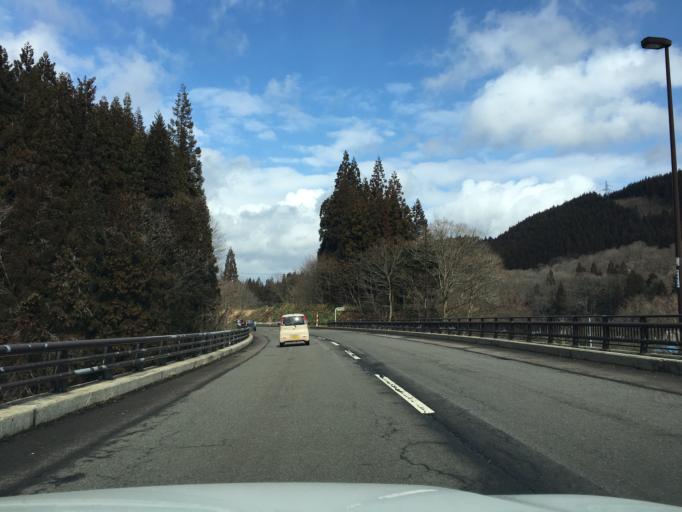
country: JP
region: Akita
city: Takanosu
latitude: 40.0123
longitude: 140.2788
